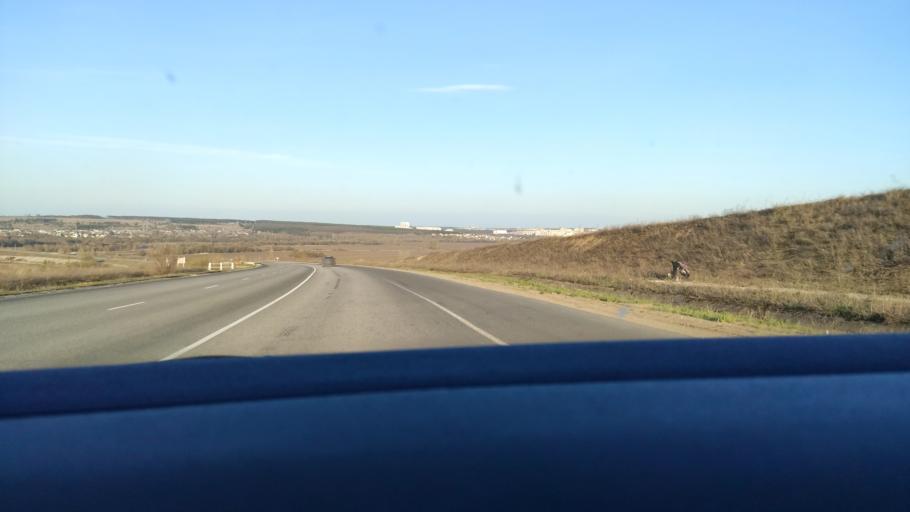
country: RU
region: Voronezj
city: Kolodeznyy
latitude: 51.3279
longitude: 39.1505
